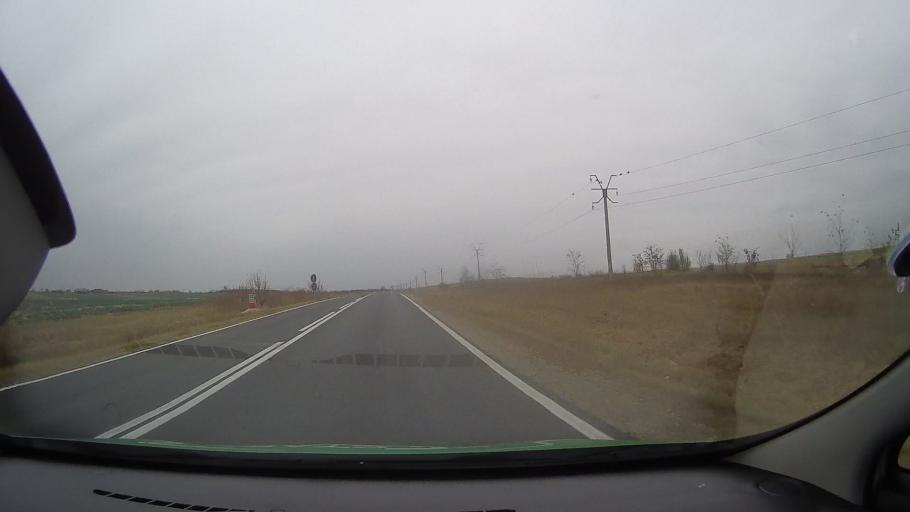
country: RO
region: Constanta
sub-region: Oras Harsova
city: Harsova
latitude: 44.6933
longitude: 27.9385
